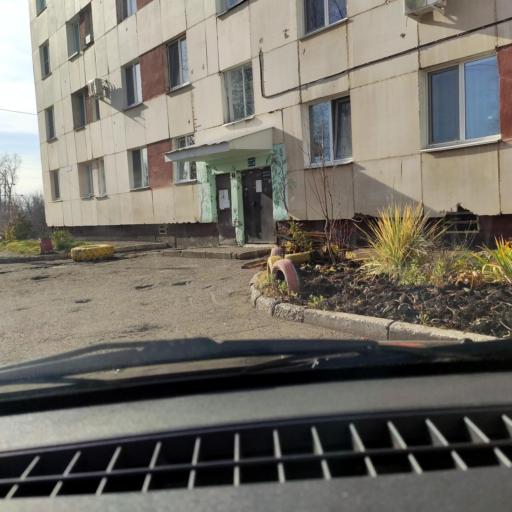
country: RU
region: Bashkortostan
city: Ufa
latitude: 54.6648
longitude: 55.9418
